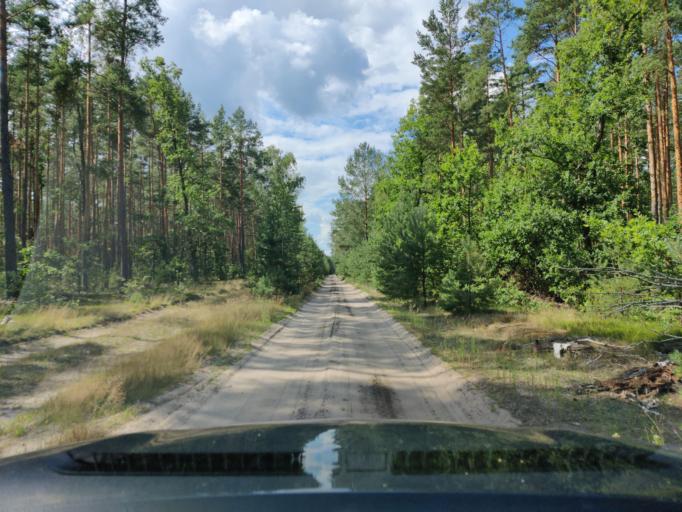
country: PL
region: Masovian Voivodeship
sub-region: Powiat pultuski
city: Pultusk
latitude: 52.7373
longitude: 21.1634
